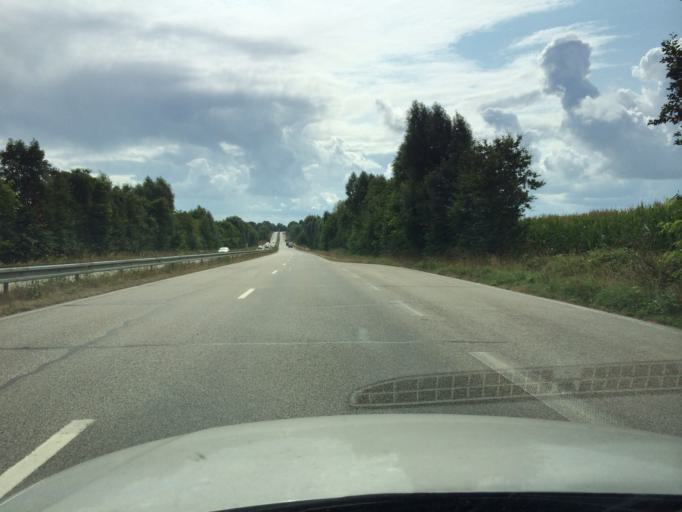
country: FR
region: Lower Normandy
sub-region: Departement de la Manche
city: Montebourg
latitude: 49.4802
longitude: -1.3844
